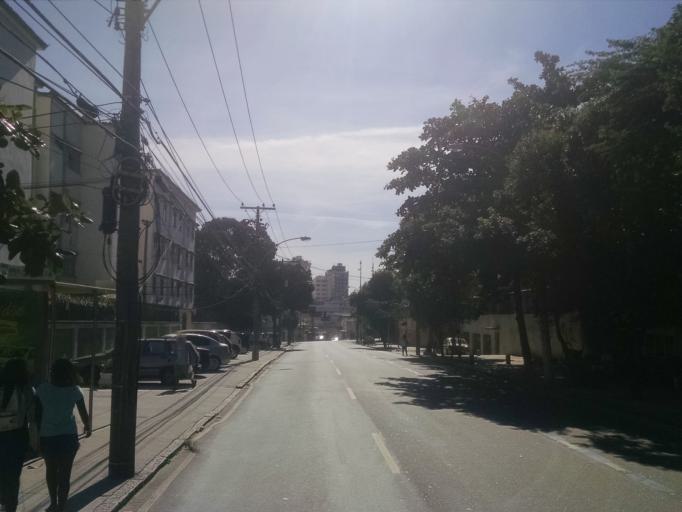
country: BR
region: Rio de Janeiro
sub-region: Rio De Janeiro
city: Rio de Janeiro
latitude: -22.9079
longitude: -43.2756
